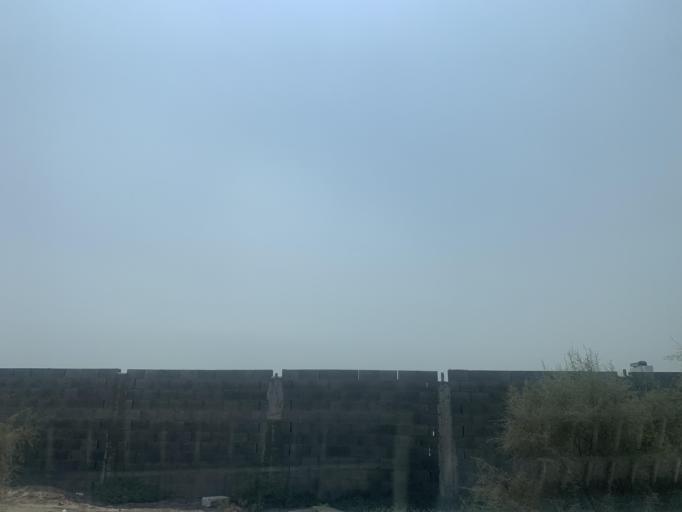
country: BH
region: Central Governorate
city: Madinat Hamad
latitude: 26.1296
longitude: 50.4672
